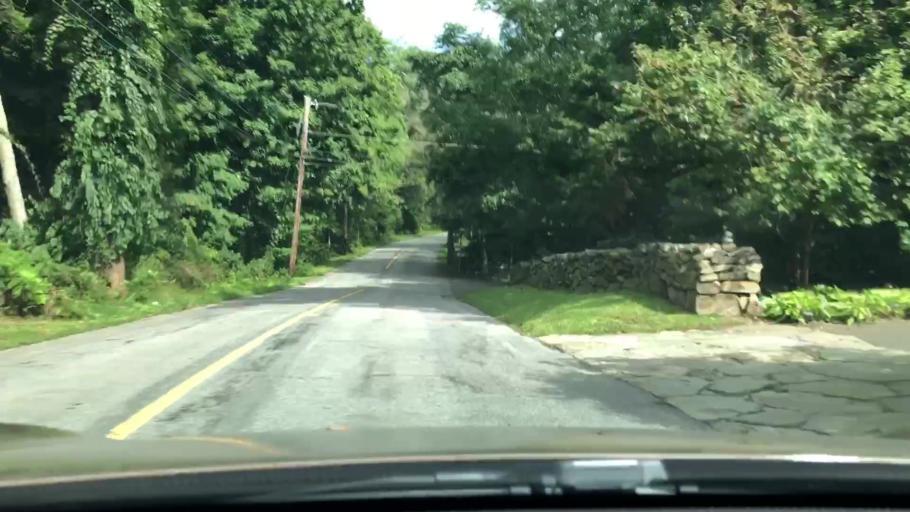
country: US
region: Connecticut
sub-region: Fairfield County
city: Darien
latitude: 41.1122
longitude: -73.4772
